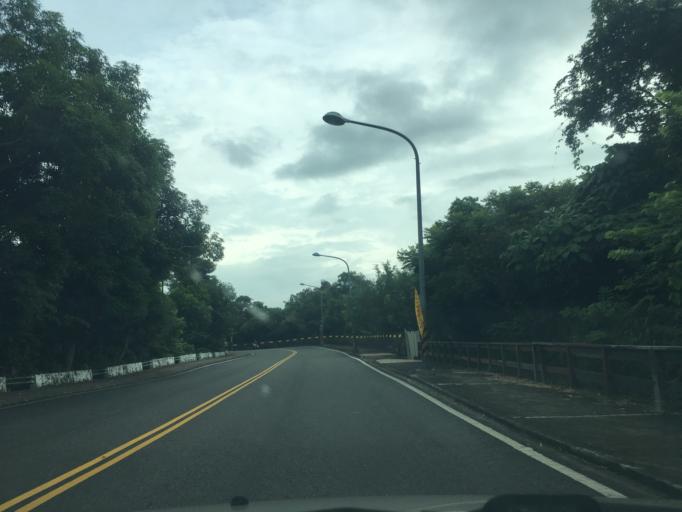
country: TW
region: Taiwan
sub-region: Changhua
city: Chang-hua
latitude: 24.0681
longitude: 120.5656
